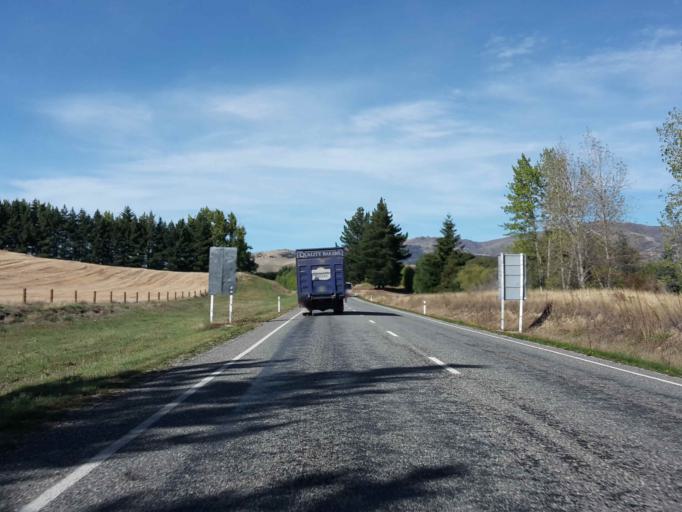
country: NZ
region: Otago
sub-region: Queenstown-Lakes District
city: Wanaka
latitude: -44.7115
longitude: 169.2083
